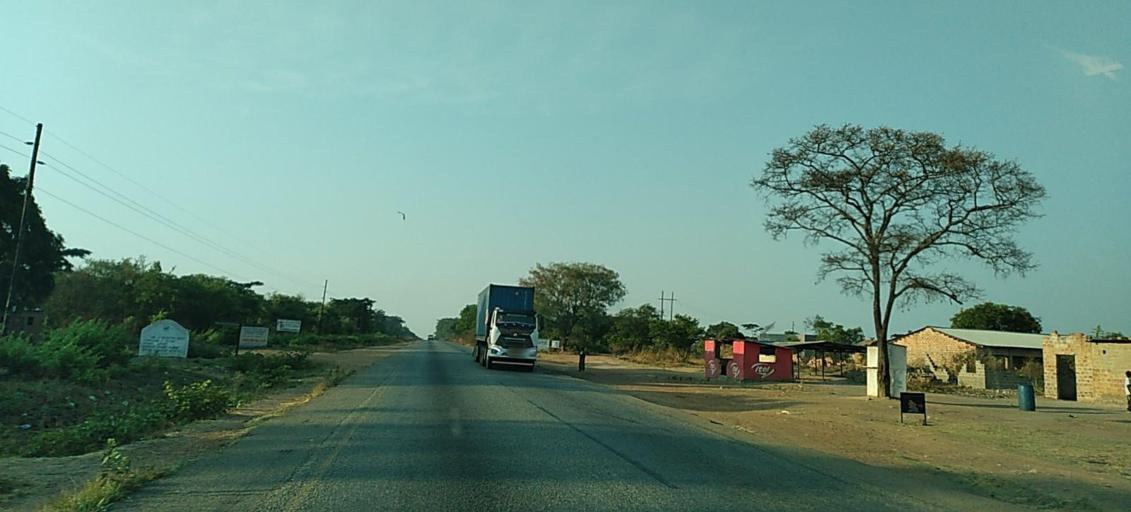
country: ZM
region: Copperbelt
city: Ndola
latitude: -13.2177
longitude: 28.6813
